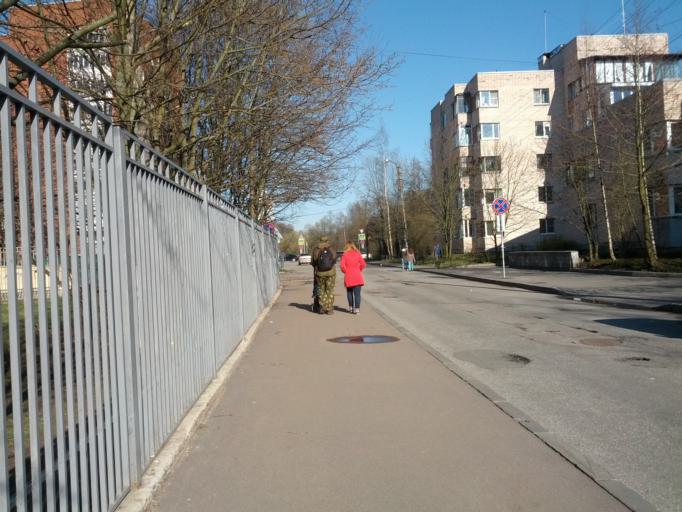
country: RU
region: St.-Petersburg
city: Sestroretsk
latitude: 60.0892
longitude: 29.9520
